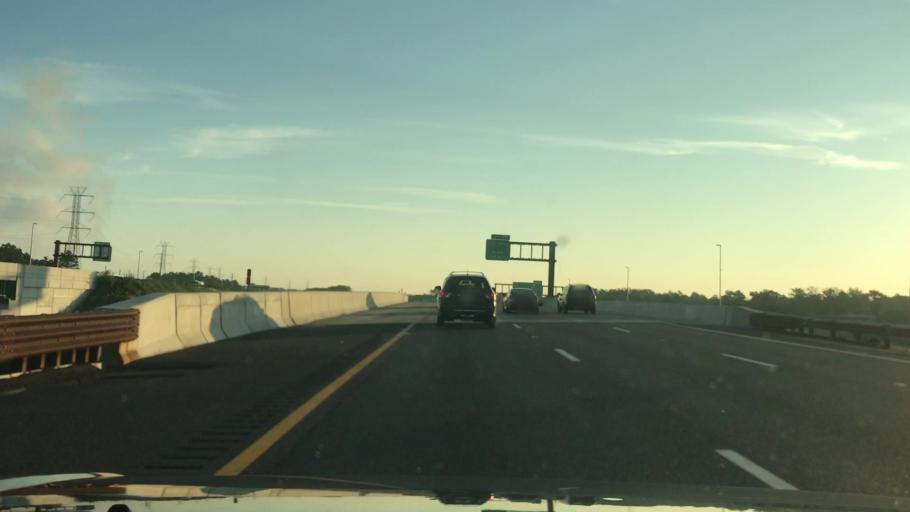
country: US
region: New Jersey
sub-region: Ocean County
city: Leisure Village
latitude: 40.0542
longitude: -74.1683
